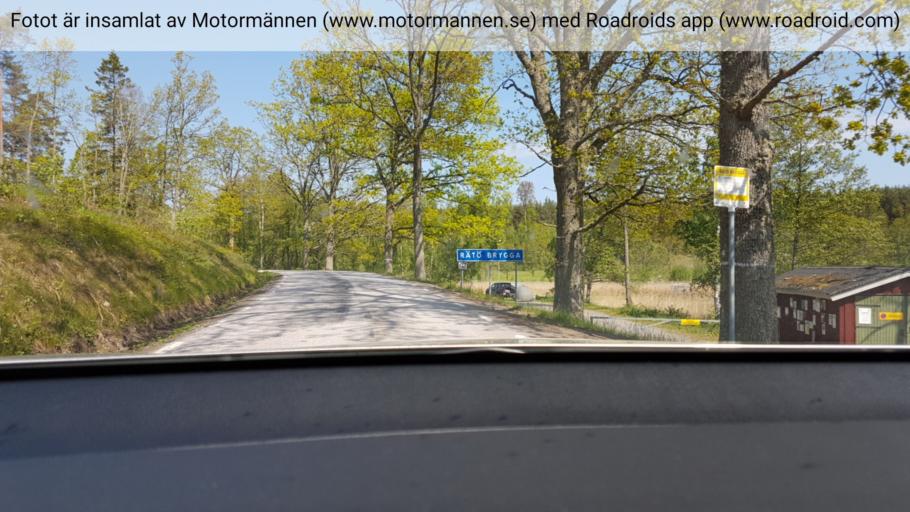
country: SE
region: Kalmar
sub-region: Vasterviks Kommun
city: Vaestervik
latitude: 57.8389
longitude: 16.5412
